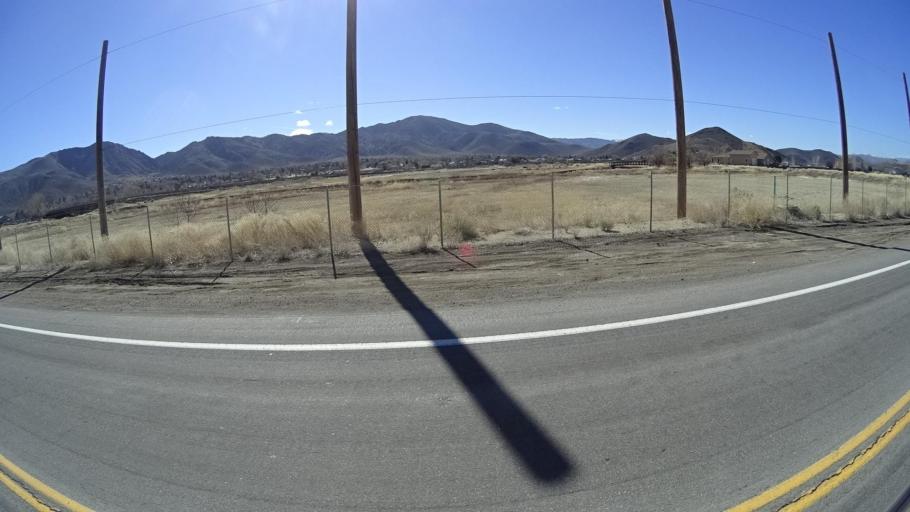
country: US
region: Nevada
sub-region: Washoe County
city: Sparks
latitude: 39.4967
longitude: -119.7337
